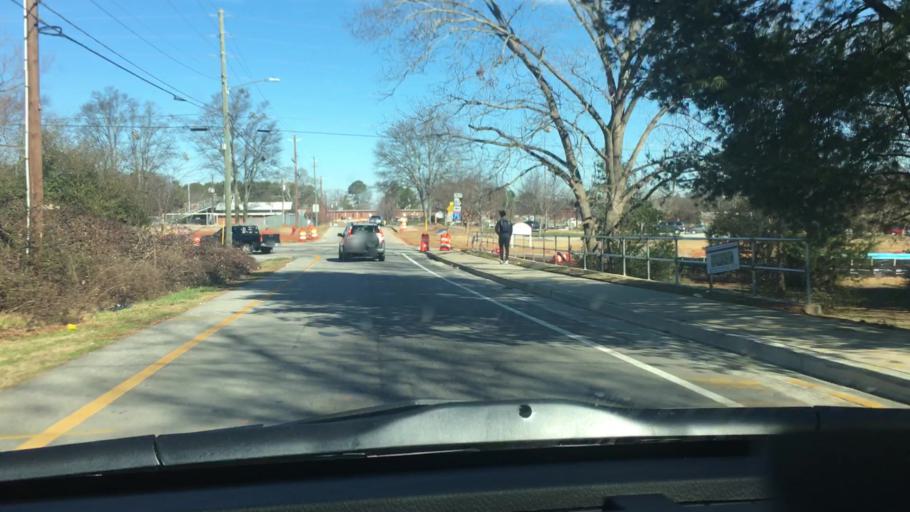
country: US
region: Georgia
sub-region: Henry County
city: McDonough
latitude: 33.4472
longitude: -84.1359
